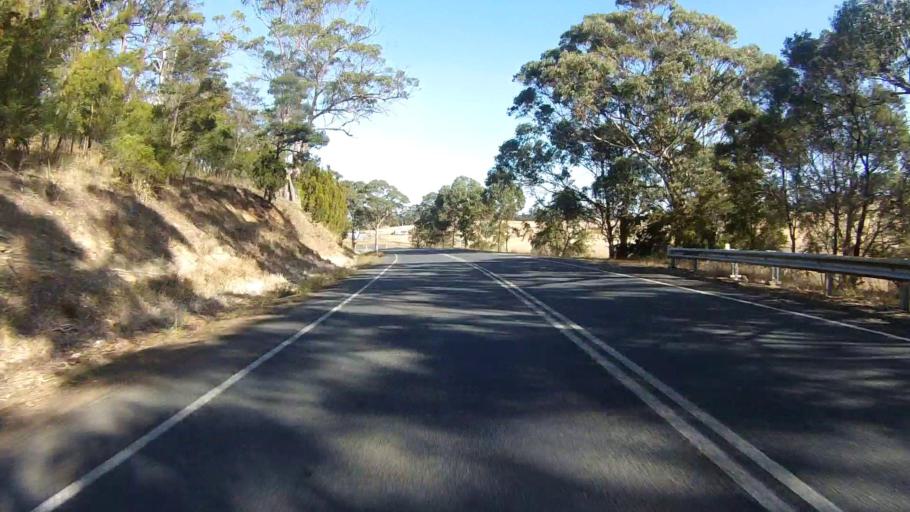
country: AU
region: Tasmania
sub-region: Sorell
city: Sorell
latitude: -42.7091
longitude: 147.5103
